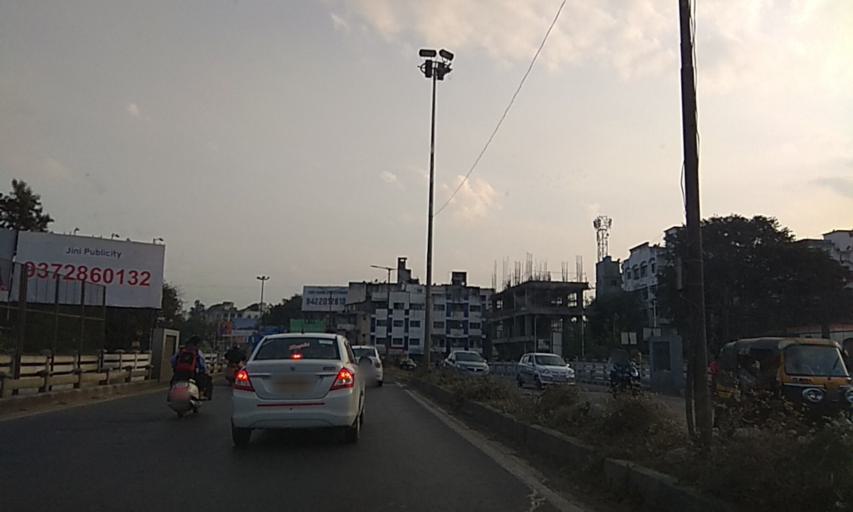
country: IN
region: Maharashtra
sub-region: Pune Division
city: Khadki
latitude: 18.5677
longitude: 73.8116
